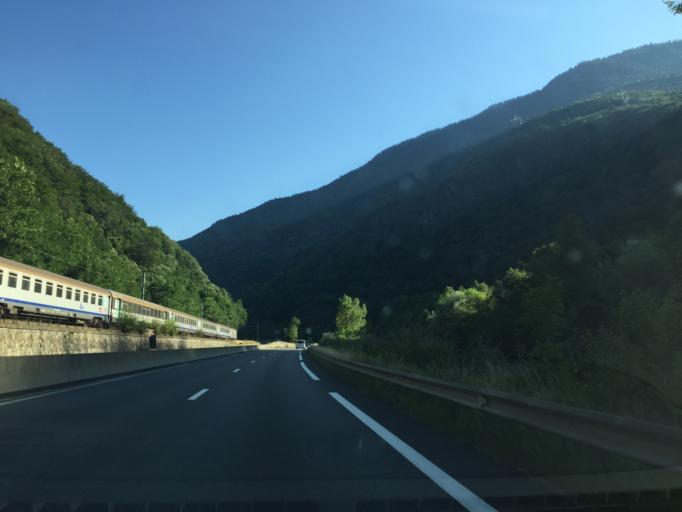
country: FR
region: Rhone-Alpes
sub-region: Departement de la Savoie
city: Aigueblanche
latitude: 45.5501
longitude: 6.4687
